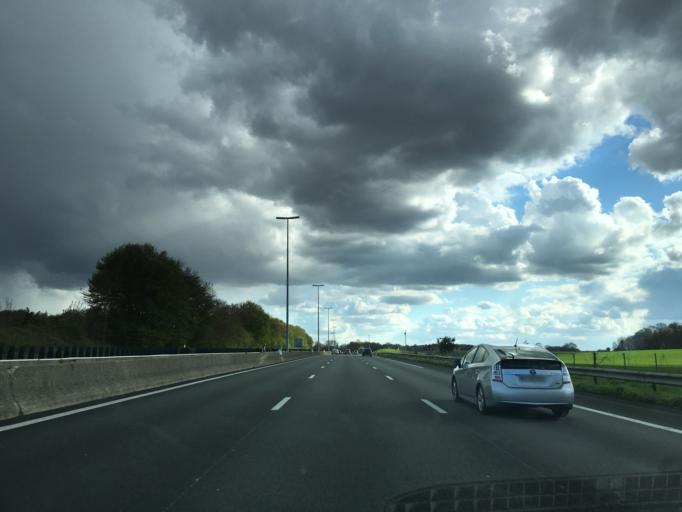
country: FR
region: Ile-de-France
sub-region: Departement du Val-d'Oise
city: Survilliers
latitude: 49.1158
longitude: 2.5547
